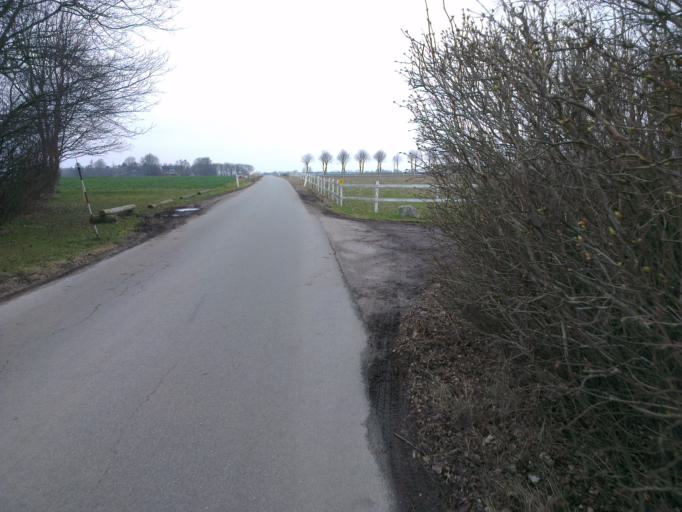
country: DK
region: Capital Region
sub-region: Egedal Kommune
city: Olstykke
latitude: 55.8133
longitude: 12.1132
